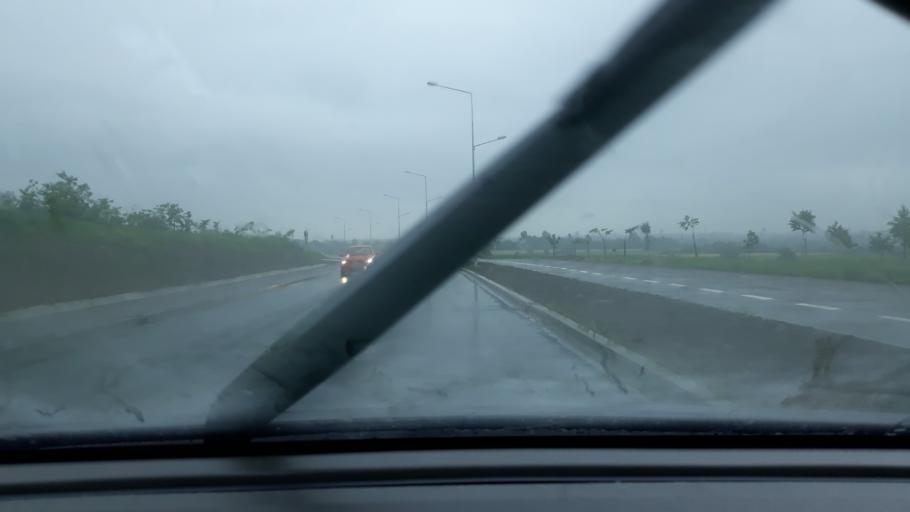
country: RO
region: Bihor
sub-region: Comuna Biharea
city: Biharea
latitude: 47.1057
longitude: 21.9073
